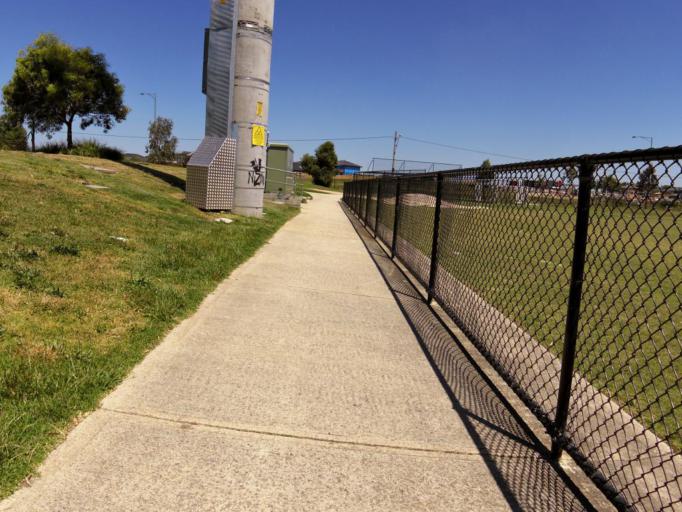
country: AU
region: Victoria
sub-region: Casey
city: Berwick
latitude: -38.0740
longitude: 145.3379
